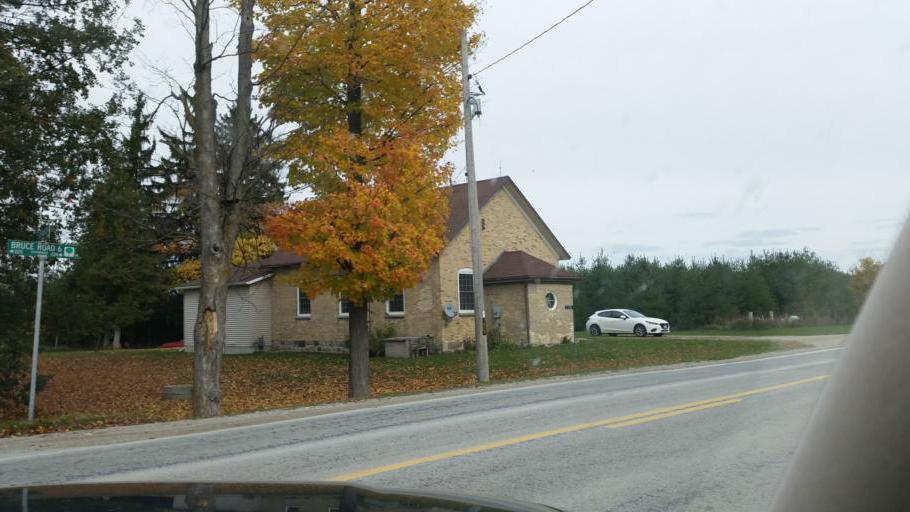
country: CA
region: Ontario
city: Wingham
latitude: 43.9935
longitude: -81.3369
